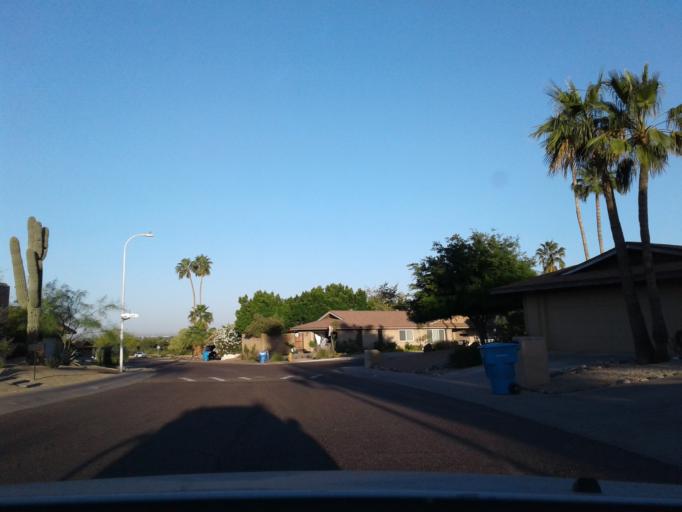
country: US
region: Arizona
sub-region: Maricopa County
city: Paradise Valley
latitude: 33.5351
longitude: -112.0327
